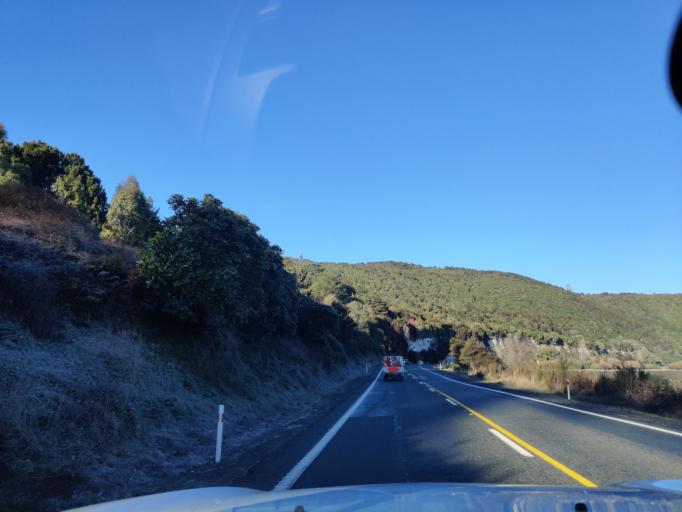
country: NZ
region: Waikato
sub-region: Taupo District
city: Taupo
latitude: -38.8728
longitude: 176.0038
